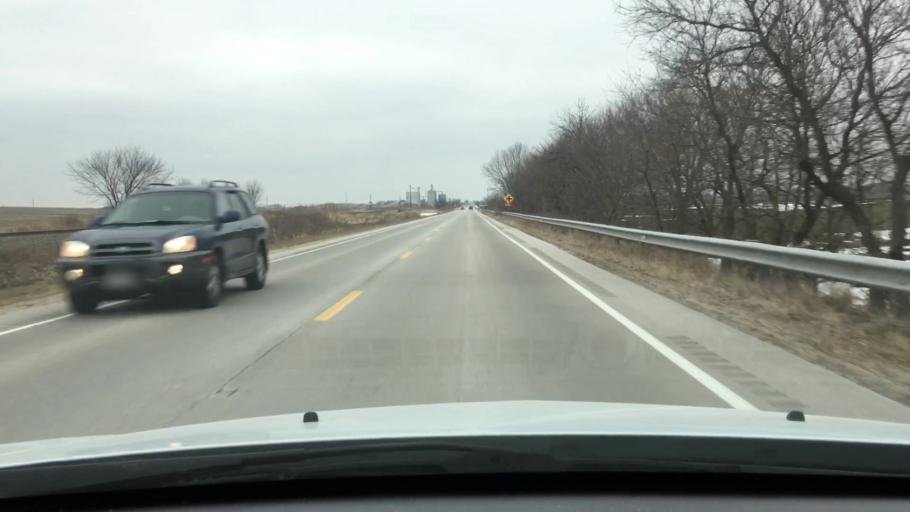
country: US
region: Illinois
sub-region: DeKalb County
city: Waterman
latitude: 41.7694
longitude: -88.7311
